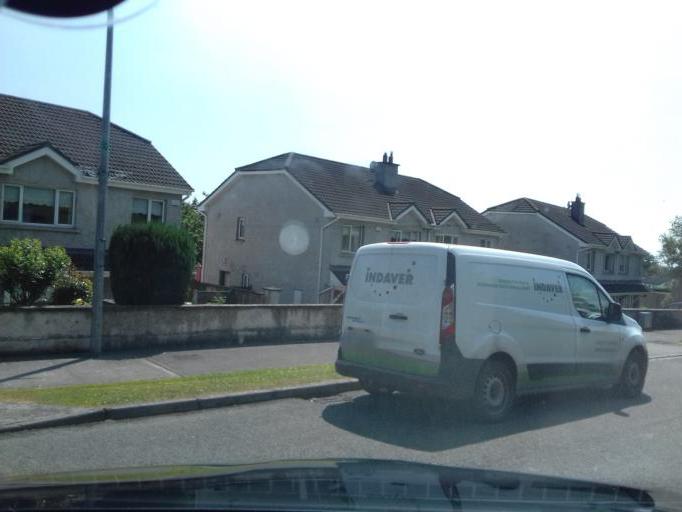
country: IE
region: Leinster
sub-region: An Mhi
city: Slane
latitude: 53.7145
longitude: -6.5382
